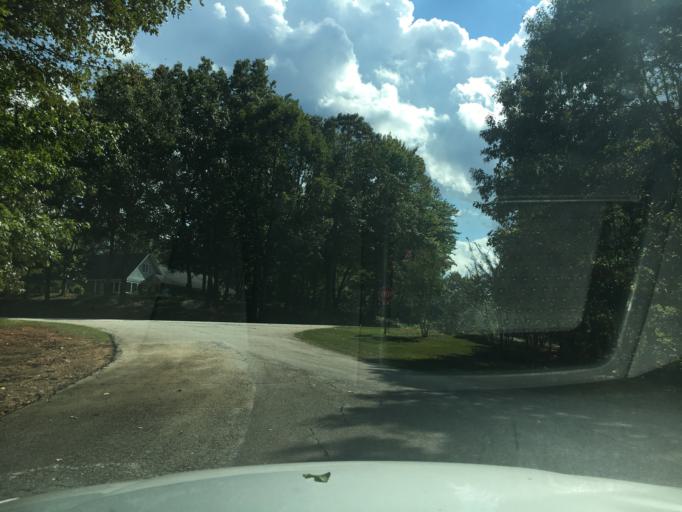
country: US
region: South Carolina
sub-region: Oconee County
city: Utica
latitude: 34.7194
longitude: -82.9249
